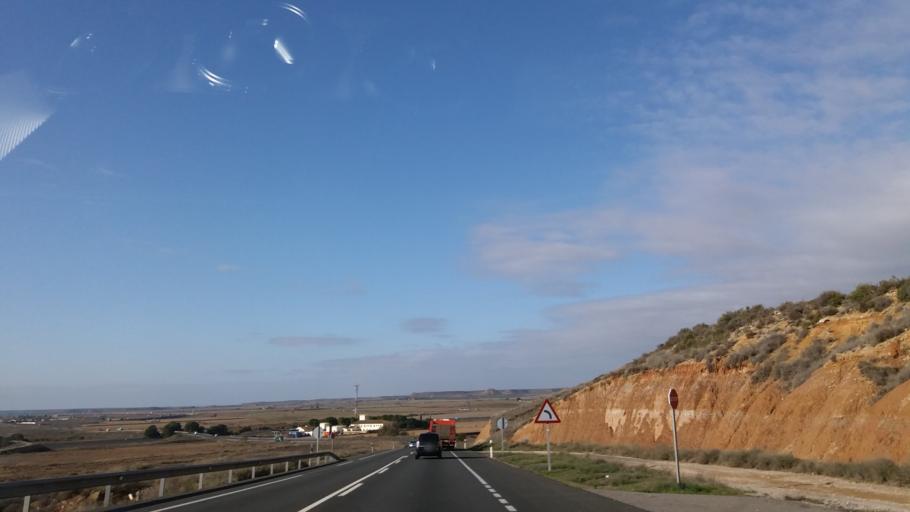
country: ES
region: Aragon
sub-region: Provincia de Huesca
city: Candasnos
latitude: 41.5132
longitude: 0.0962
